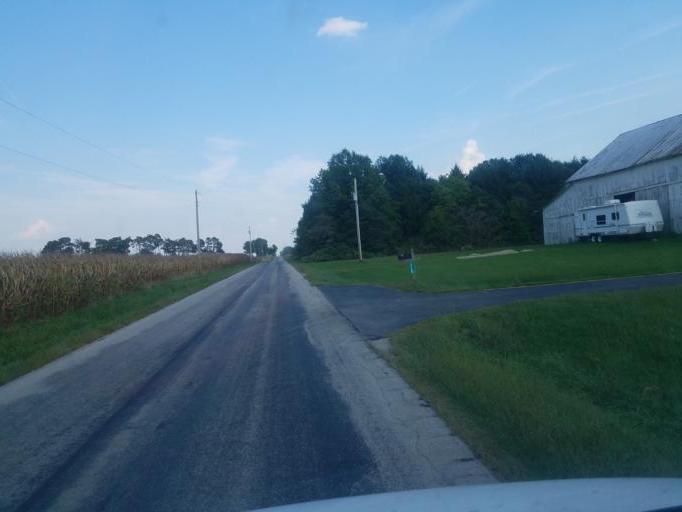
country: US
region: Ohio
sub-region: Hardin County
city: Forest
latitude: 40.9049
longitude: -83.4845
